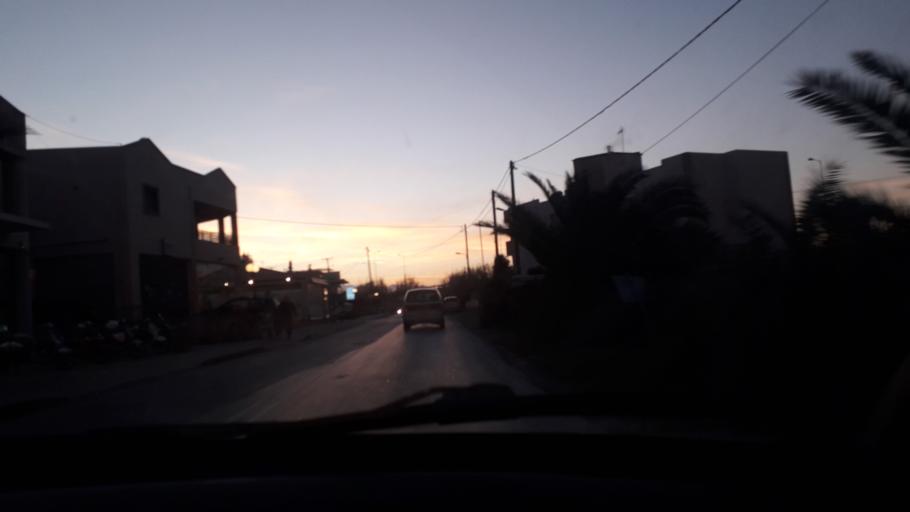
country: GR
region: Crete
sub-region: Nomos Rethymnis
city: Rethymno
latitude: 35.3807
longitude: 24.5838
